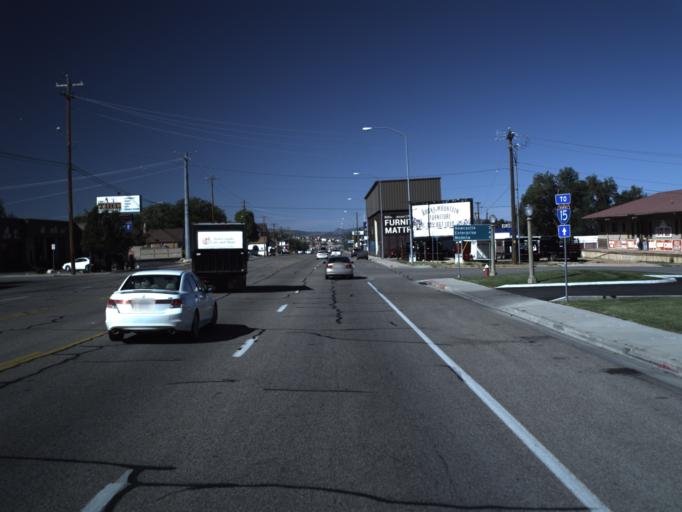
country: US
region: Utah
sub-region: Iron County
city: Cedar City
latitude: 37.6810
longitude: -113.0628
